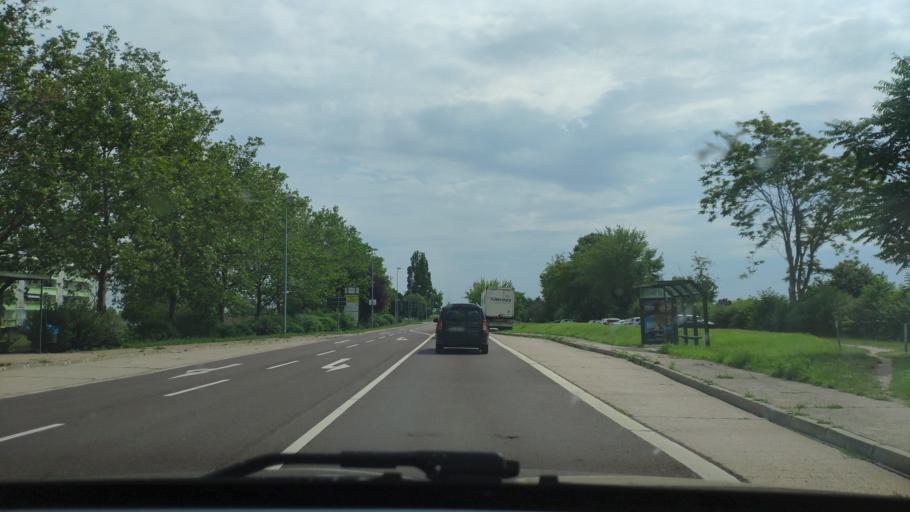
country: DE
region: Saxony-Anhalt
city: Bernburg
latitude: 51.7767
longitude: 11.7481
